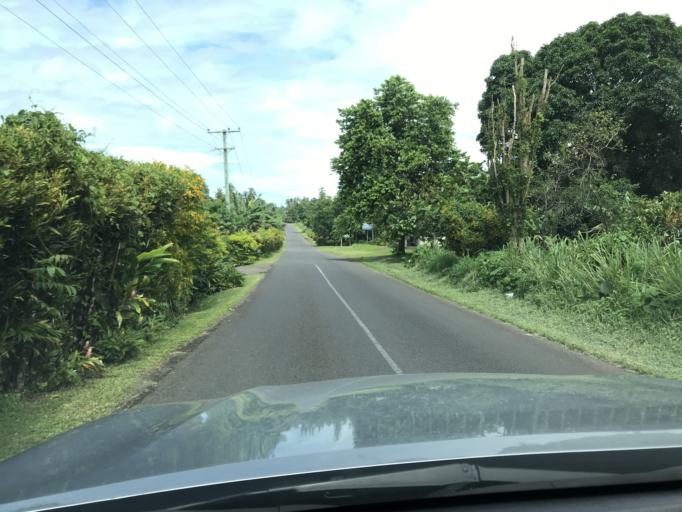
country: WS
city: Fasito`outa
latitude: -13.8577
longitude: -171.9017
